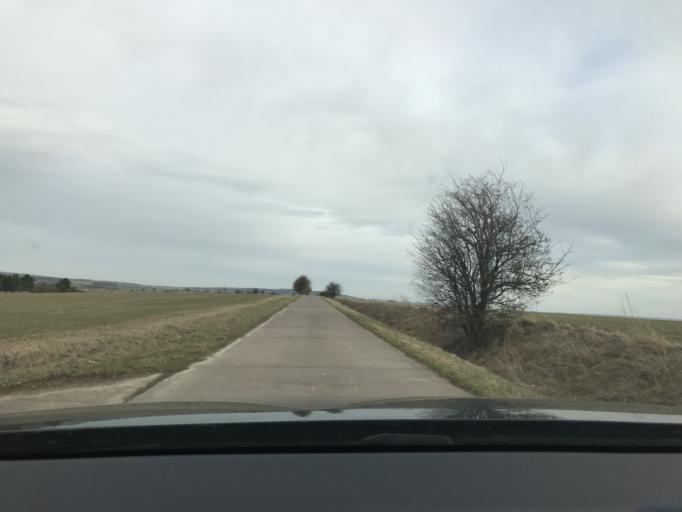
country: DE
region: Thuringia
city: Anrode
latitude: 51.2504
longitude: 10.3916
